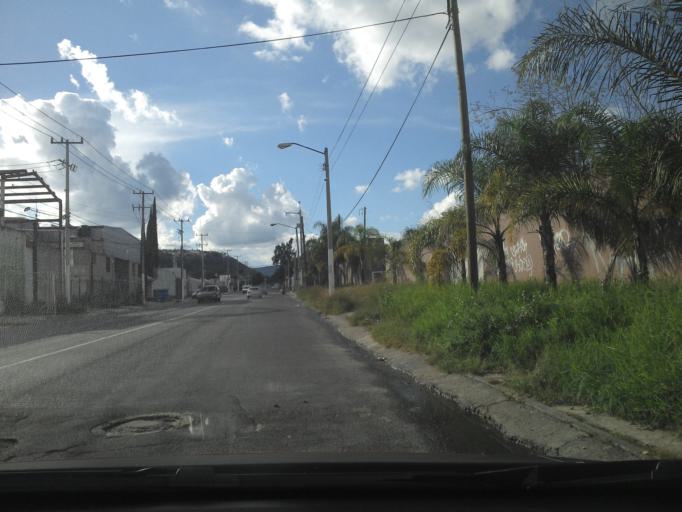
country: MX
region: Jalisco
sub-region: Tlajomulco de Zuniga
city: Palomar
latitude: 20.6169
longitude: -103.4474
